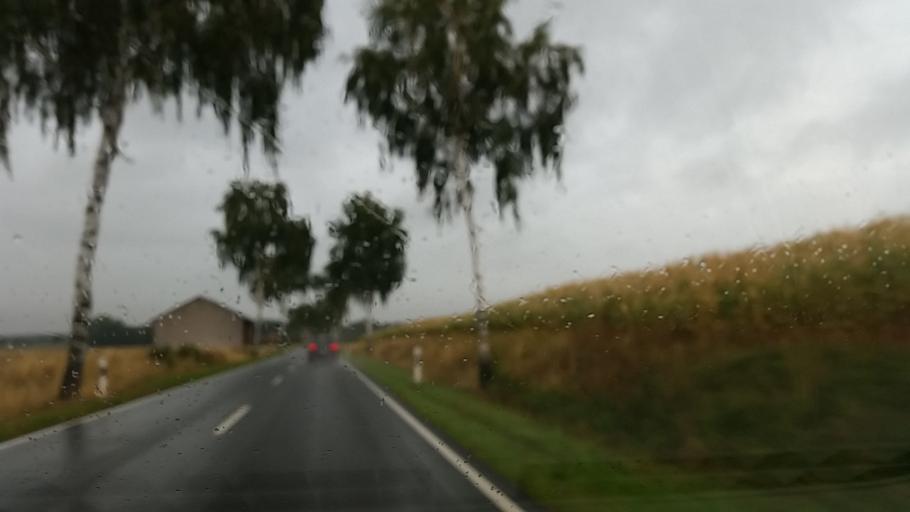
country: DE
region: Saxony-Anhalt
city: Jubar
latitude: 52.6557
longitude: 10.8427
